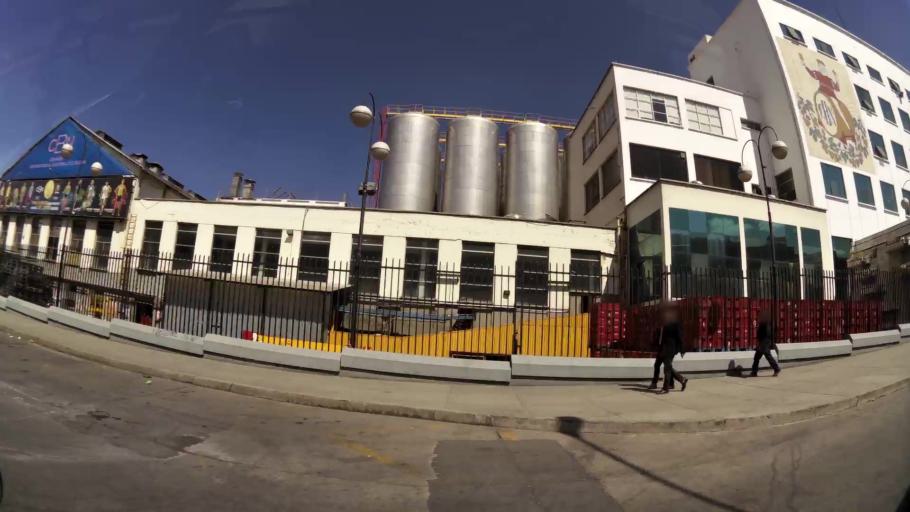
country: BO
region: La Paz
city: La Paz
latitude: -16.4898
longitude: -68.1427
